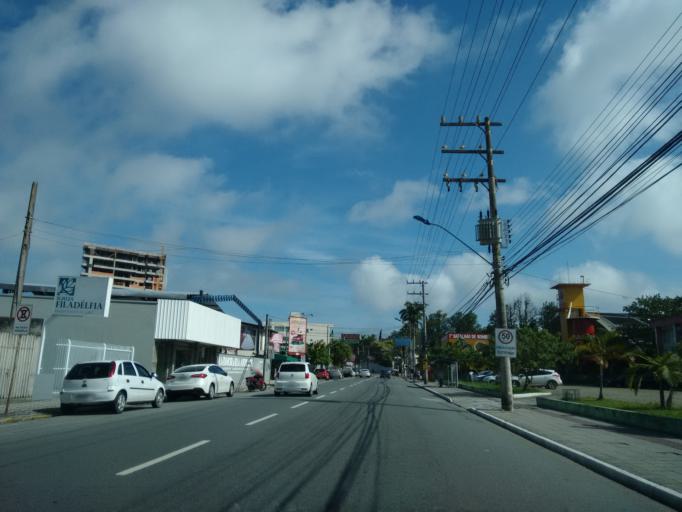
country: BR
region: Santa Catarina
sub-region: Itajai
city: Itajai
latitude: -26.9213
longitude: -48.6533
